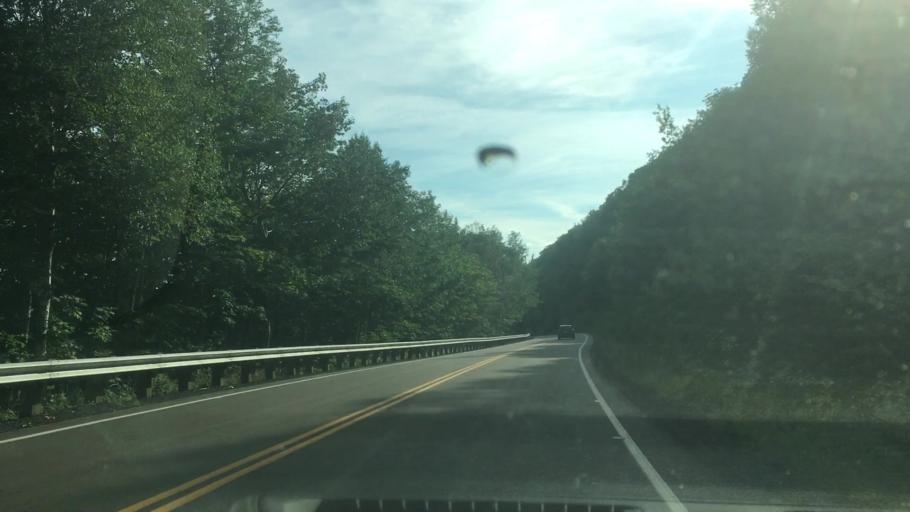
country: CA
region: Nova Scotia
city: Sydney Mines
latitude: 46.8246
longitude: -60.6252
